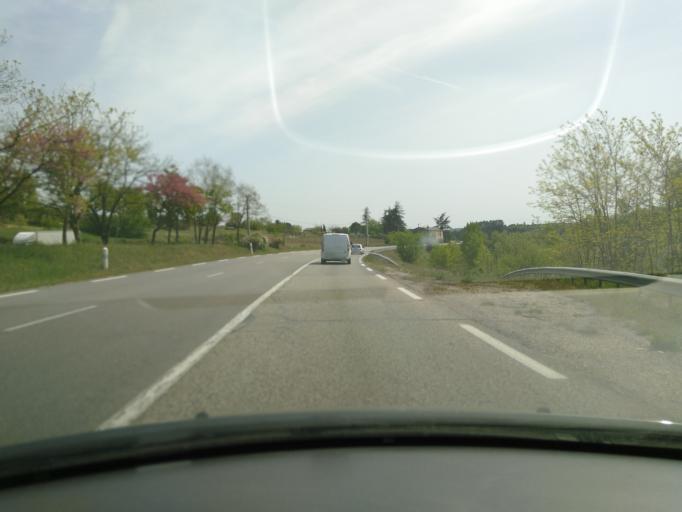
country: FR
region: Rhone-Alpes
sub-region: Departement de l'Ardeche
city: Alba-la-Romaine
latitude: 44.5780
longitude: 4.5775
